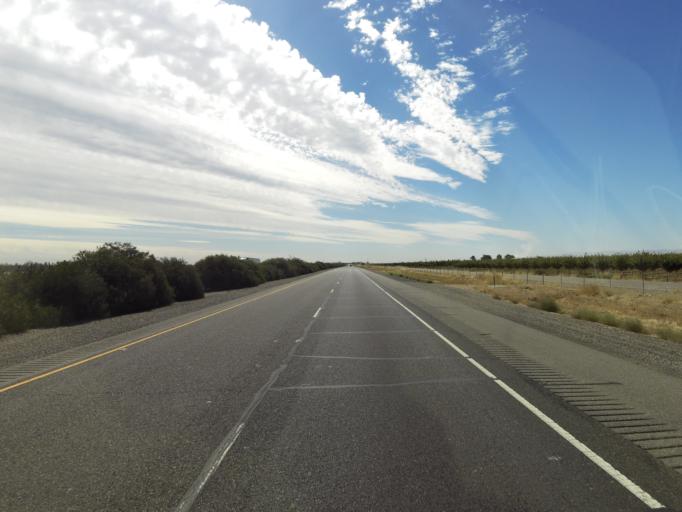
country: US
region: California
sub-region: Glenn County
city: Willows
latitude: 39.5504
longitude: -122.2150
